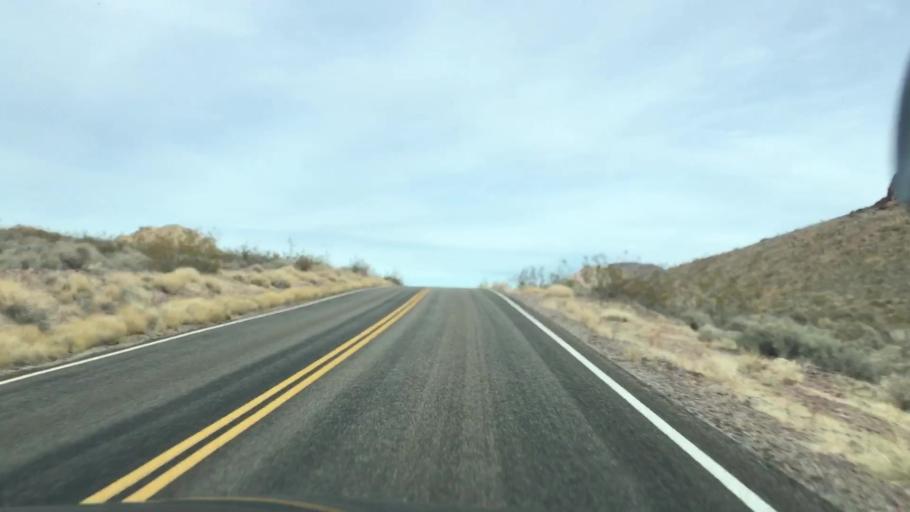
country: US
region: Nevada
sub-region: Nye County
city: Beatty
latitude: 36.7855
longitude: -116.9310
